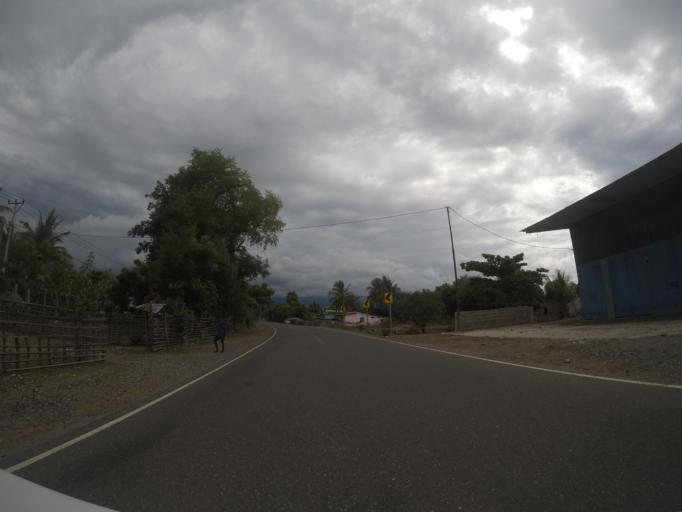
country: TL
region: Liquica
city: Maubara
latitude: -8.7674
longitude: 125.0994
